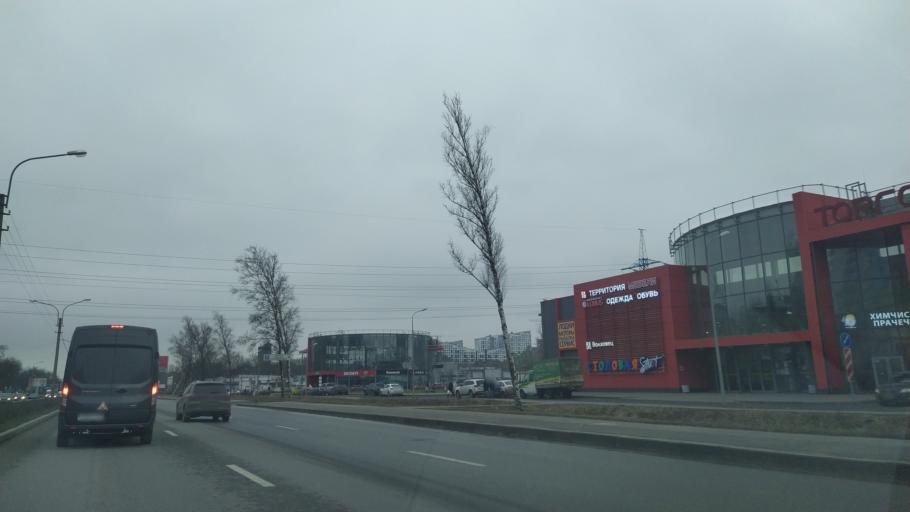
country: RU
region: St.-Petersburg
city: Kupchino
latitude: 59.8331
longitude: 30.3401
